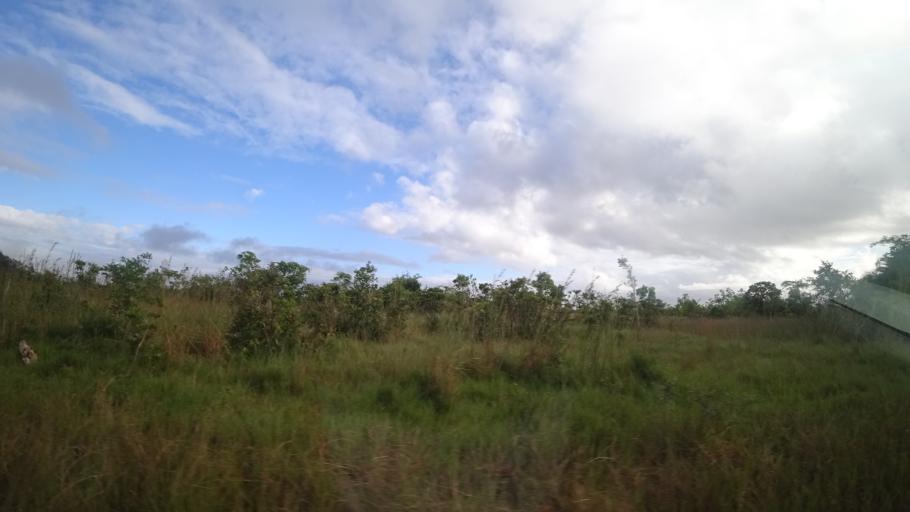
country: MZ
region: Sofala
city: Beira
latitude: -19.6910
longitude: 35.0412
